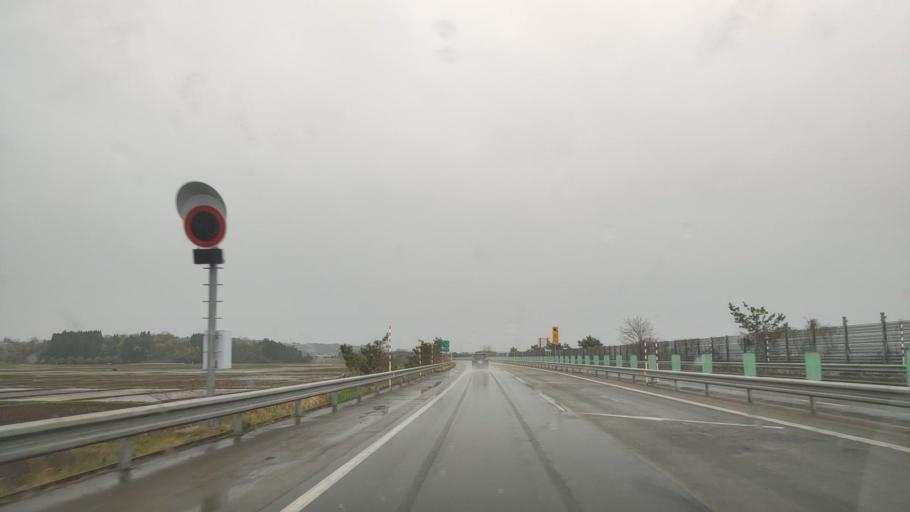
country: JP
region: Akita
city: Noshiromachi
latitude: 40.1827
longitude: 140.0701
